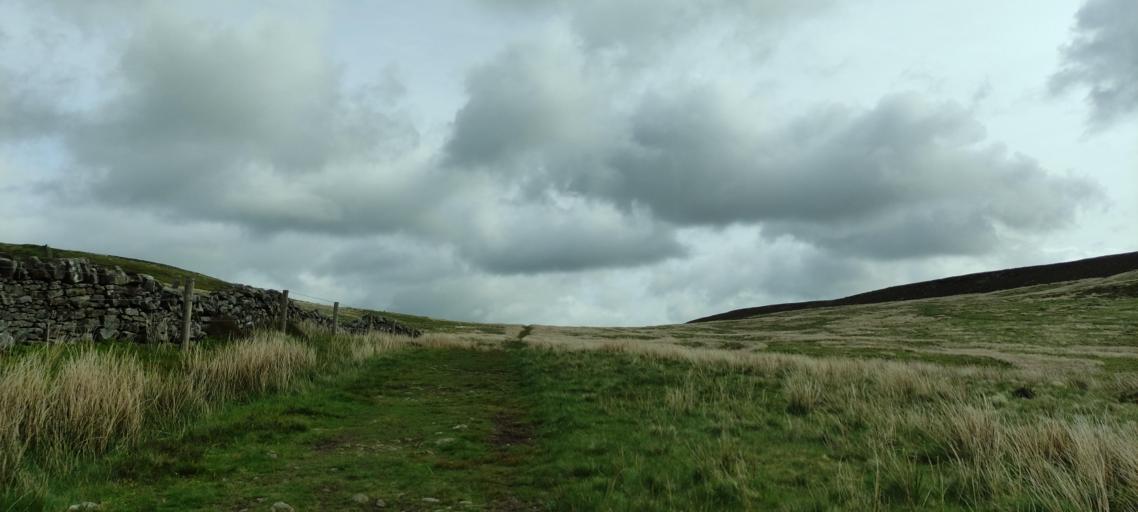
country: GB
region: England
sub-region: Cumbria
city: Brampton
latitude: 54.8957
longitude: -2.6696
